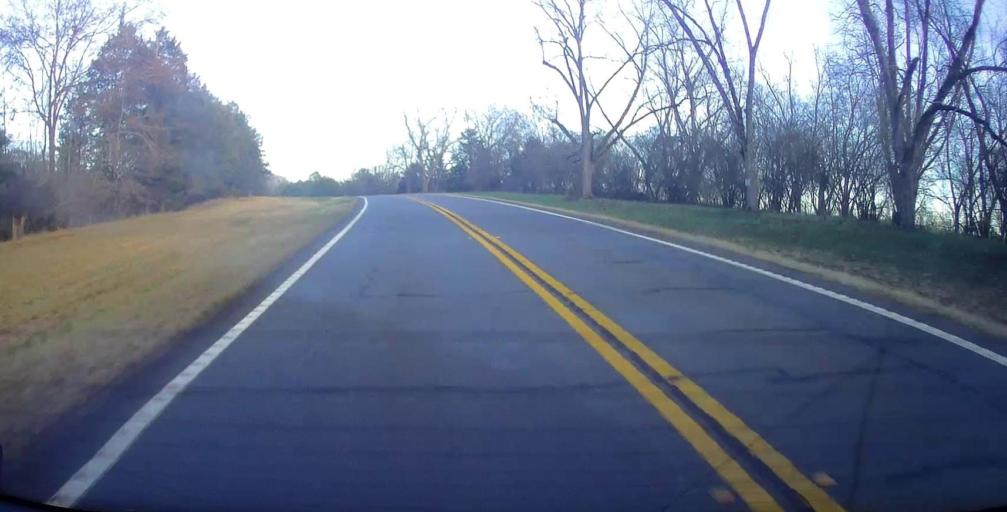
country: US
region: Georgia
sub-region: Talbot County
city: Talbotton
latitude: 32.7844
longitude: -84.5238
